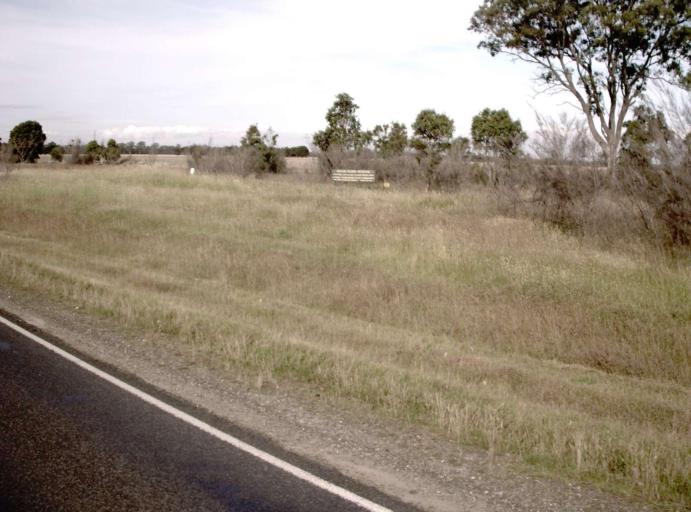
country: AU
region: Victoria
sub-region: Latrobe
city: Traralgon
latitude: -38.0773
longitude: 146.6104
